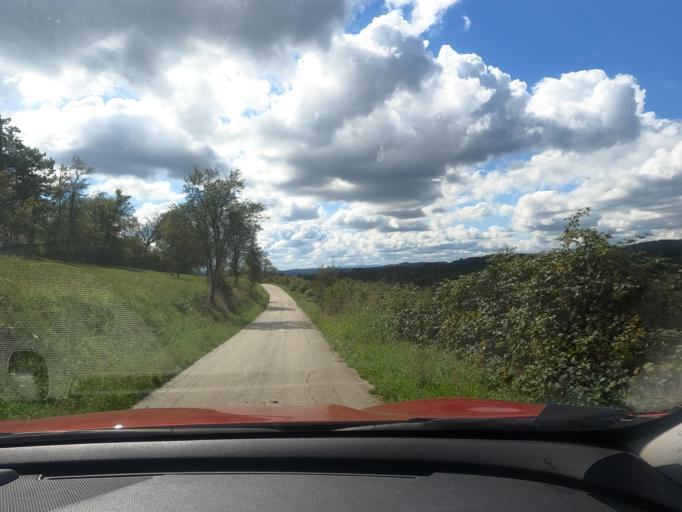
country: HR
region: Karlovacka
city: Vojnic
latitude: 45.2300
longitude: 15.7080
